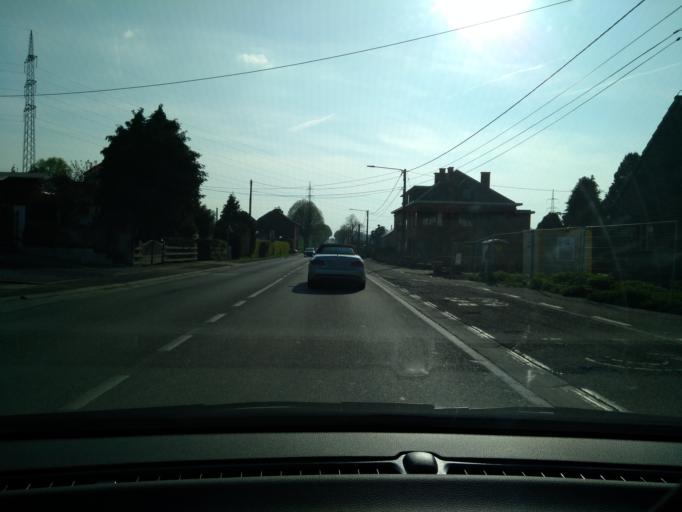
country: BE
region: Wallonia
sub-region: Province du Hainaut
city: Morlanwelz-Mariemont
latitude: 50.4462
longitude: 4.2333
